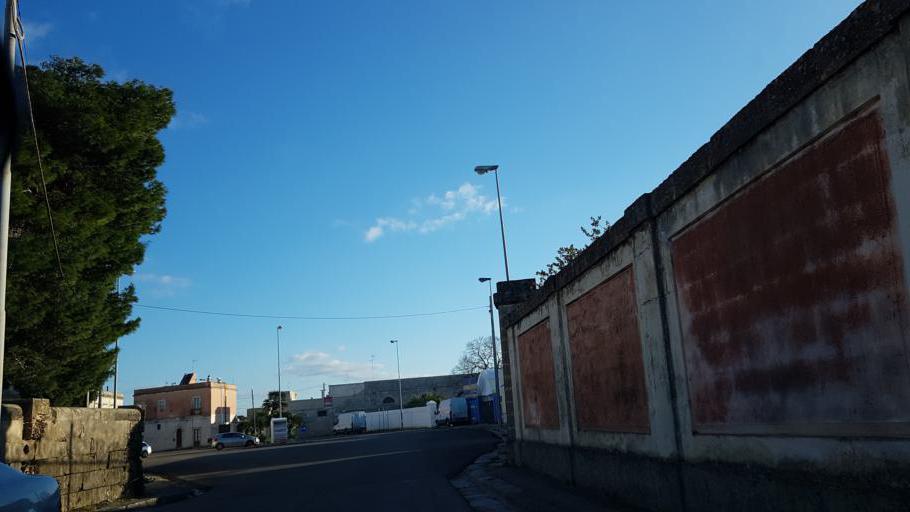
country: IT
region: Apulia
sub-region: Provincia di Lecce
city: Squinzano
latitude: 40.4397
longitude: 18.0452
